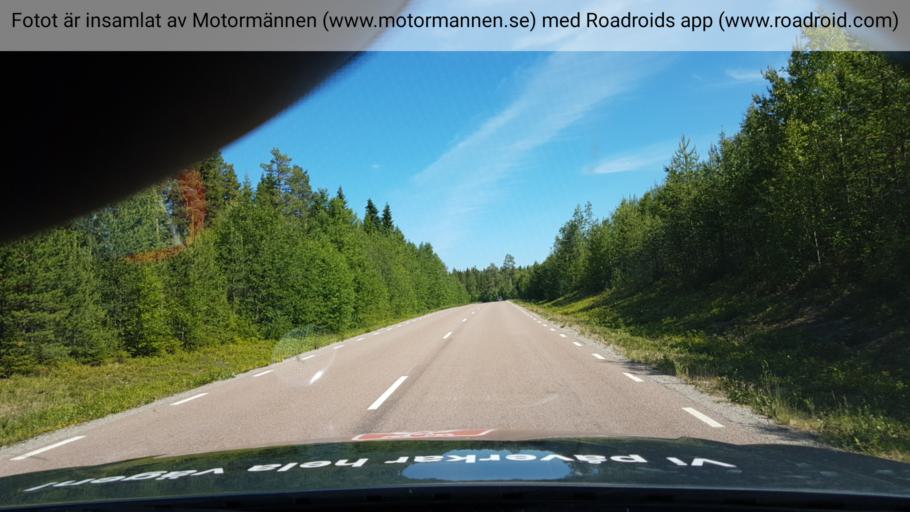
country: SE
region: Jaemtland
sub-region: Braecke Kommun
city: Braecke
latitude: 62.7508
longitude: 15.2650
